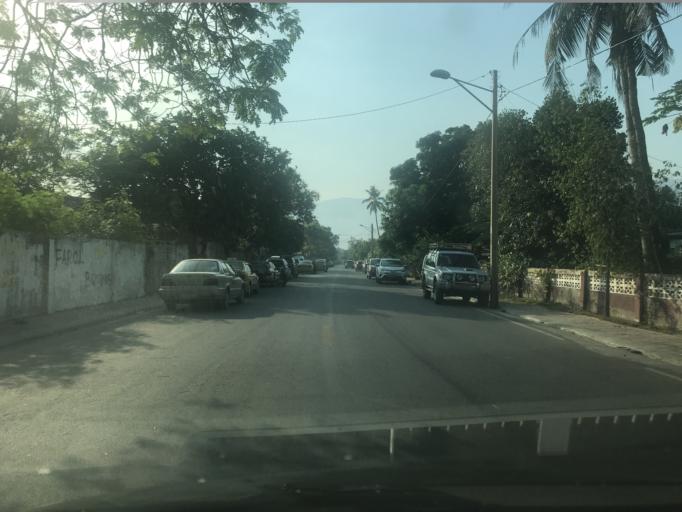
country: TL
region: Dili
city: Dili
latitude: -8.5507
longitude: 125.5692
